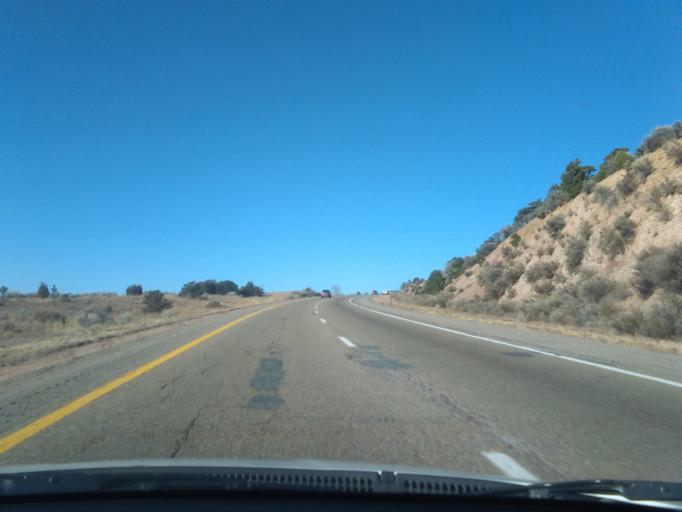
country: US
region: New Mexico
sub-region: Santa Fe County
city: Eldorado at Santa Fe
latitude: 35.5376
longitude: -105.8556
